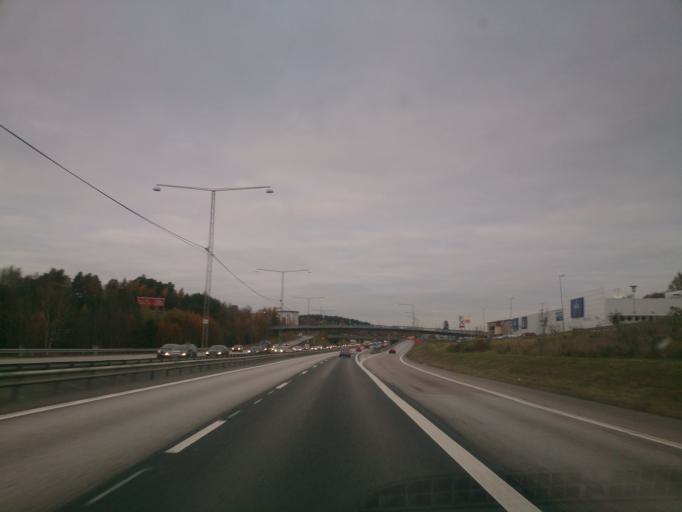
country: SE
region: Stockholm
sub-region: Upplands Vasby Kommun
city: Upplands Vaesby
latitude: 59.5103
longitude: 17.9241
